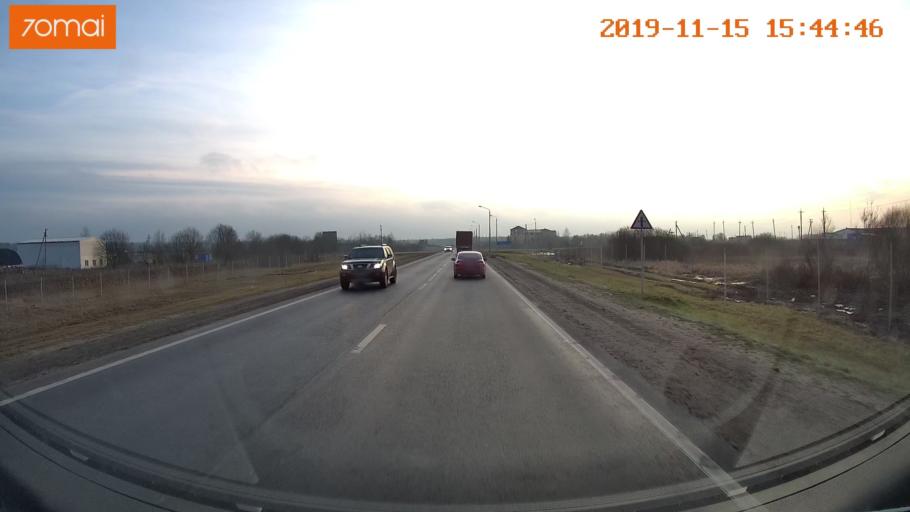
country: RU
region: Jaroslavl
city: Danilov
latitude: 57.9669
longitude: 40.0191
